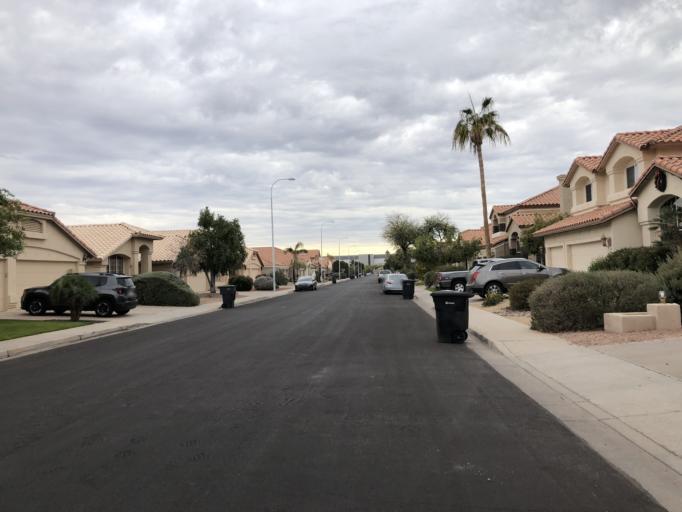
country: US
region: Arizona
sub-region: Maricopa County
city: Guadalupe
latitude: 33.3097
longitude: -111.9227
